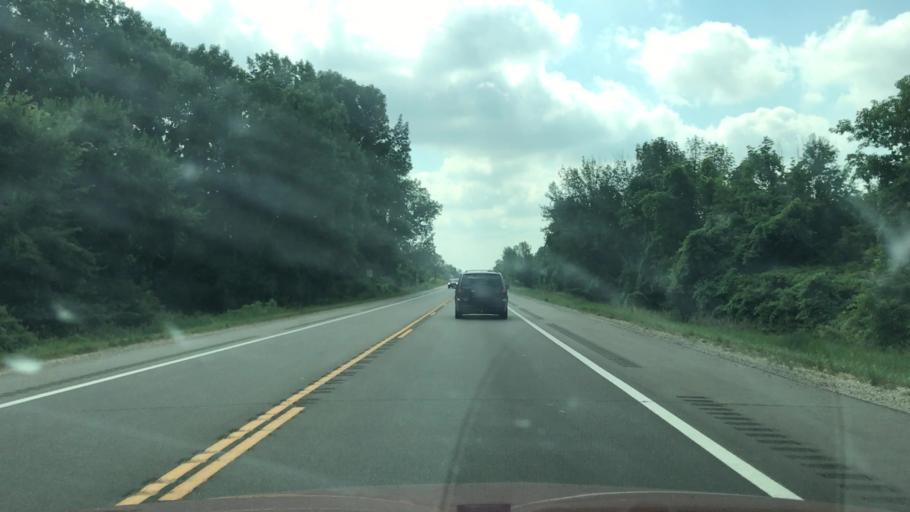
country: US
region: Michigan
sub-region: Kent County
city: Kent City
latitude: 43.2333
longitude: -85.7966
